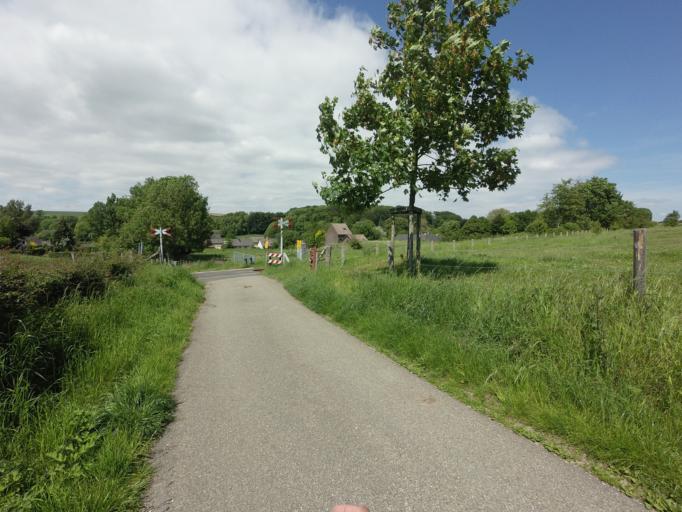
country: NL
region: Limburg
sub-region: Gemeente Voerendaal
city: Ubachsberg
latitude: 50.8226
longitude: 5.9507
